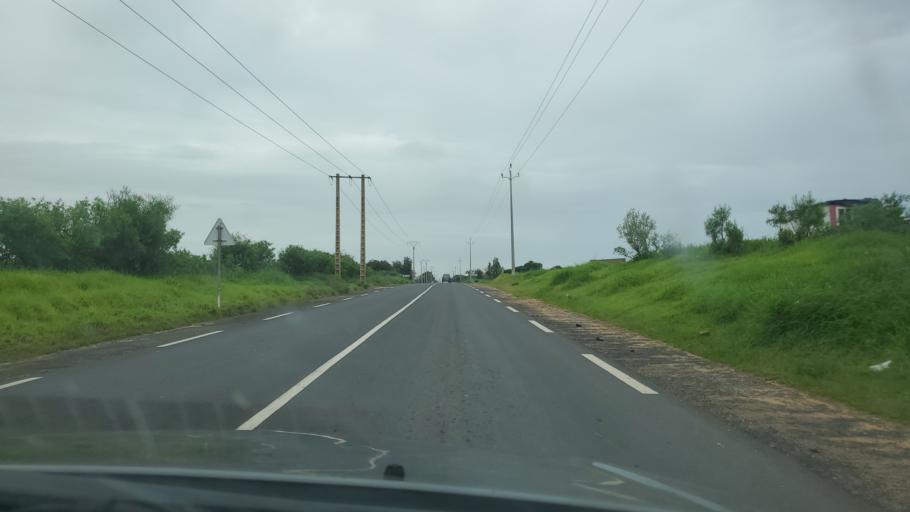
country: SN
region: Thies
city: Kayar
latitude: 15.0623
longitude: -16.9382
